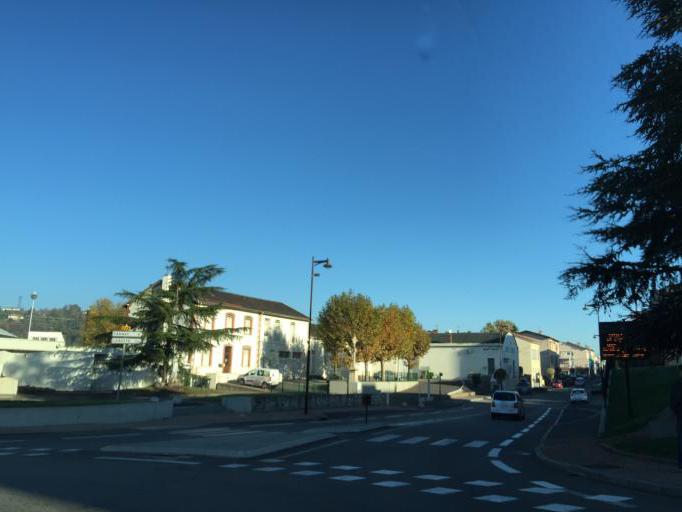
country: FR
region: Rhone-Alpes
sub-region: Departement de la Loire
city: Lorette
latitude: 45.5037
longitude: 4.5691
